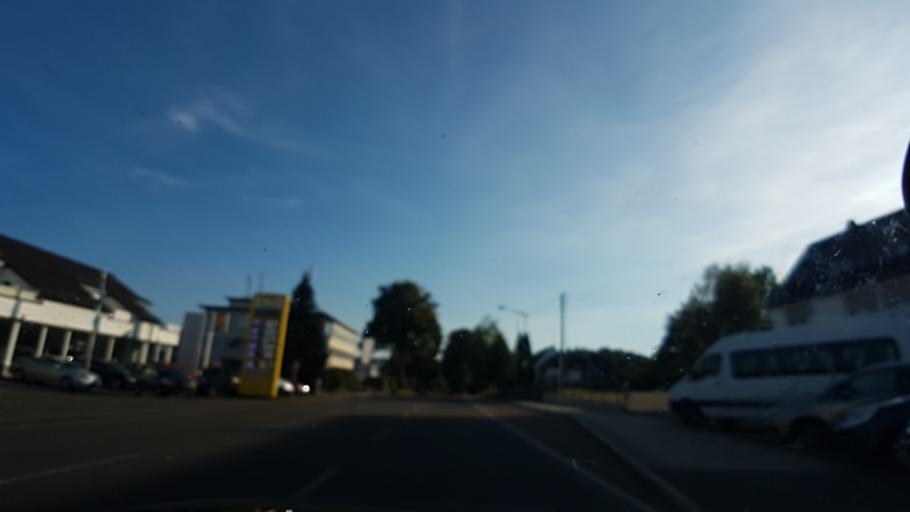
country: DE
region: North Rhine-Westphalia
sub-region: Regierungsbezirk Koln
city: Marienheide
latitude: 51.0700
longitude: 7.5591
